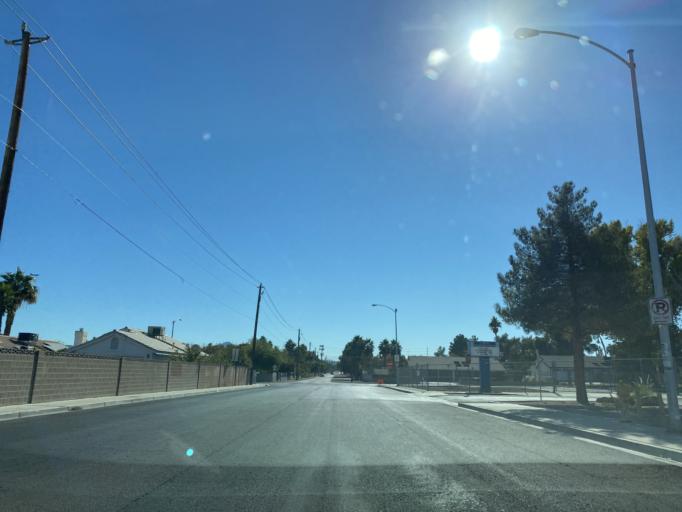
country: US
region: Nevada
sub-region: Clark County
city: Whitney
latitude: 36.0902
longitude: -115.0868
